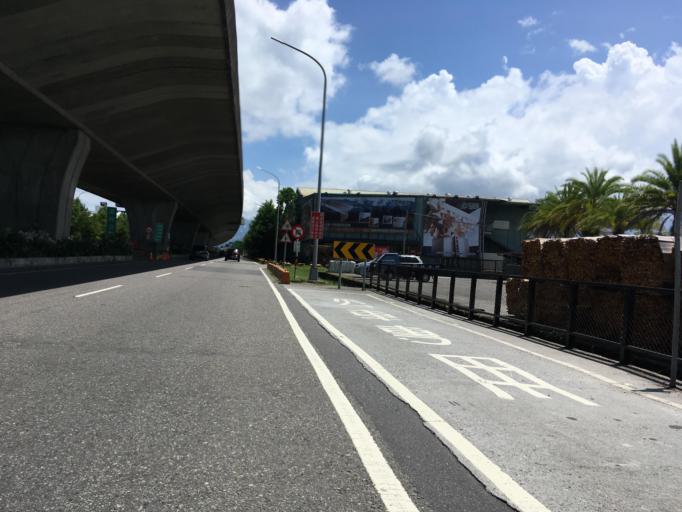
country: TW
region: Taiwan
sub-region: Yilan
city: Yilan
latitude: 24.6884
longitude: 121.7912
